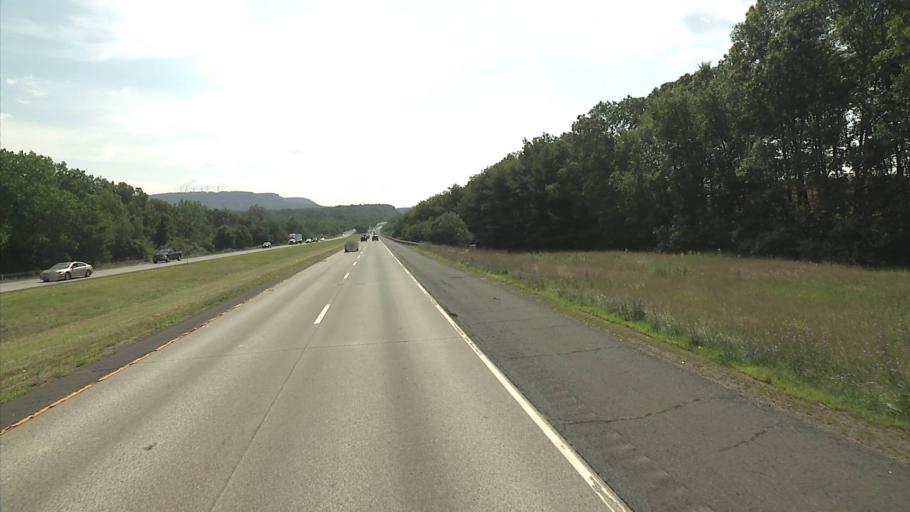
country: US
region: Connecticut
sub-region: New Haven County
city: Cheshire Village
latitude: 41.5558
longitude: -72.8786
